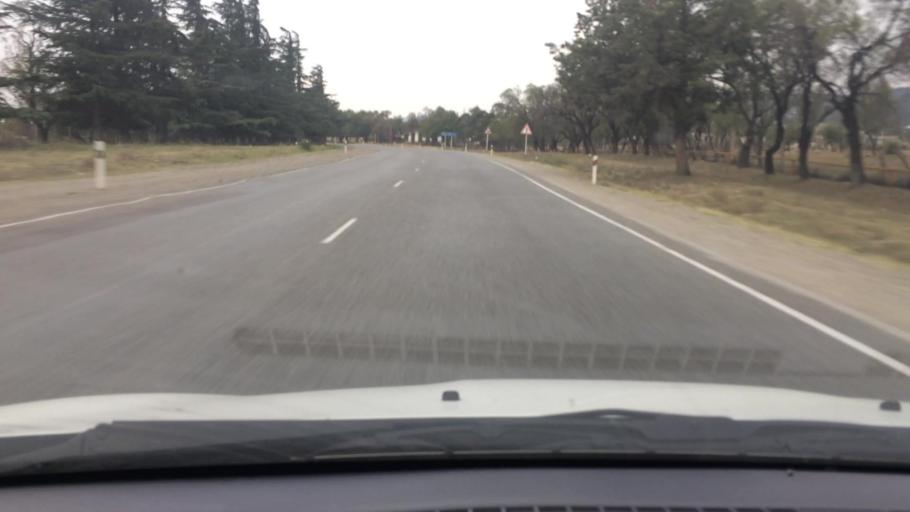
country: GE
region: T'bilisi
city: Tbilisi
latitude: 41.6433
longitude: 44.8414
